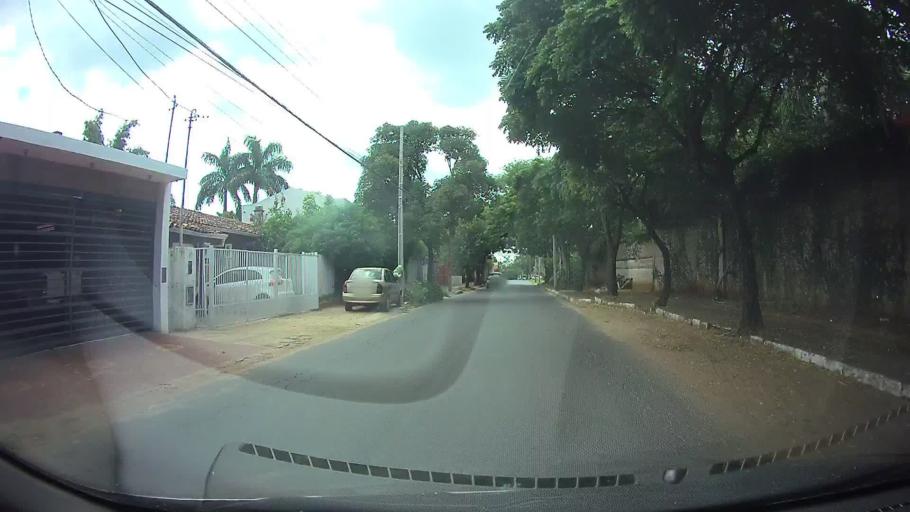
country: PY
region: Central
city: Fernando de la Mora
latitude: -25.3234
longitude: -57.5365
